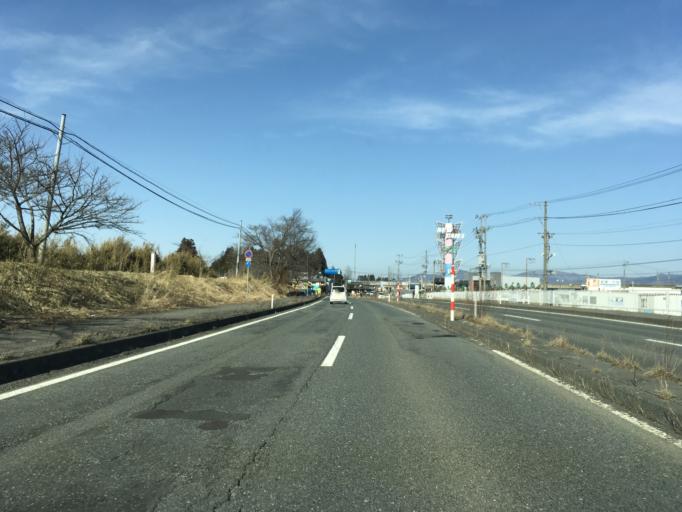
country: JP
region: Iwate
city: Hanamaki
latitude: 39.5316
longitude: 141.1648
